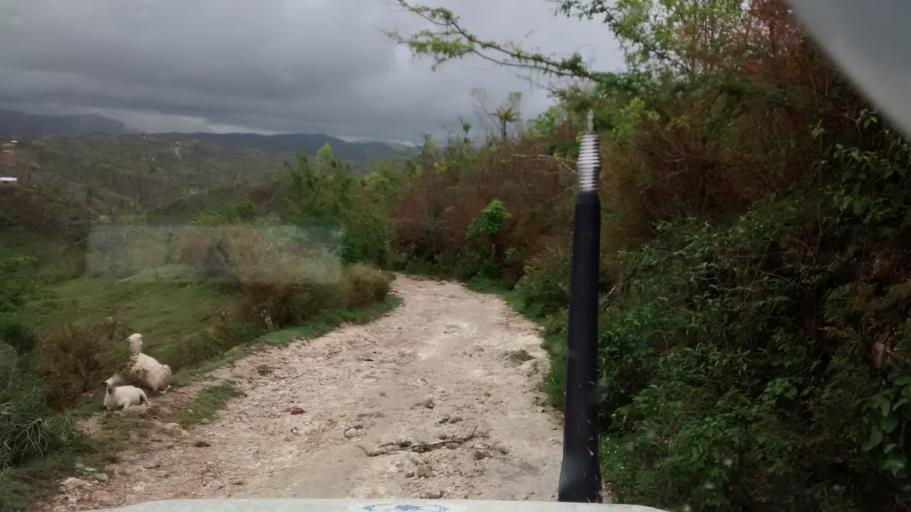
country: HT
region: Grandans
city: Jeremie
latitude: 18.5802
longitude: -74.1494
